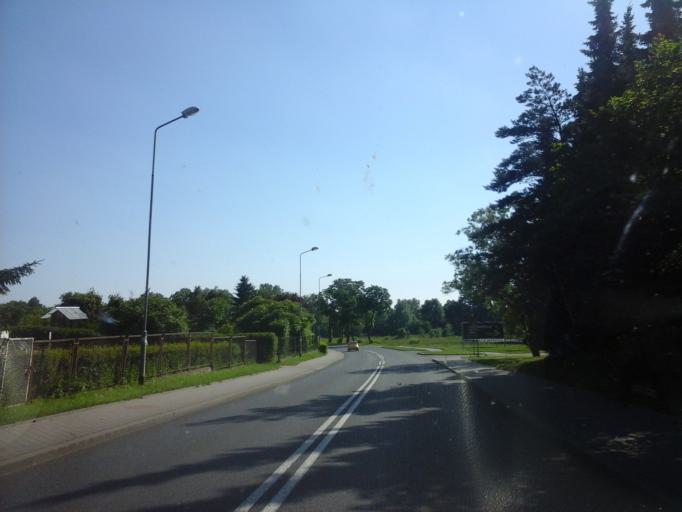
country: PL
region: West Pomeranian Voivodeship
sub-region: Powiat kolobrzeski
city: Ryman
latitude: 53.9422
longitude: 15.5263
